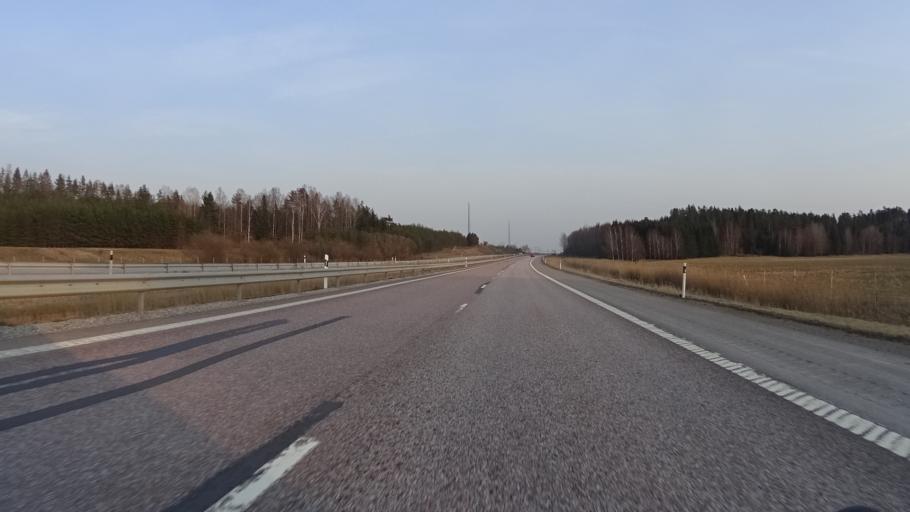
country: SE
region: Soedermanland
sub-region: Strangnas Kommun
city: Akers Styckebruk
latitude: 59.2976
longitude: 17.0920
